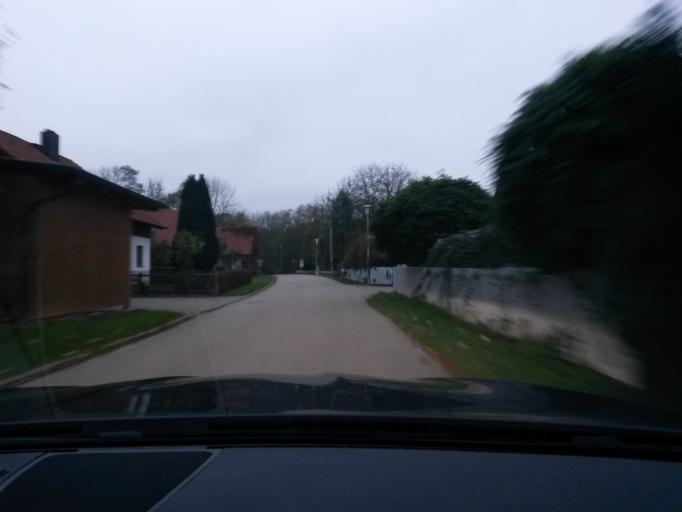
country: DE
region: Bavaria
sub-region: Lower Bavaria
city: Eching
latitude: 48.4976
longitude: 12.0300
